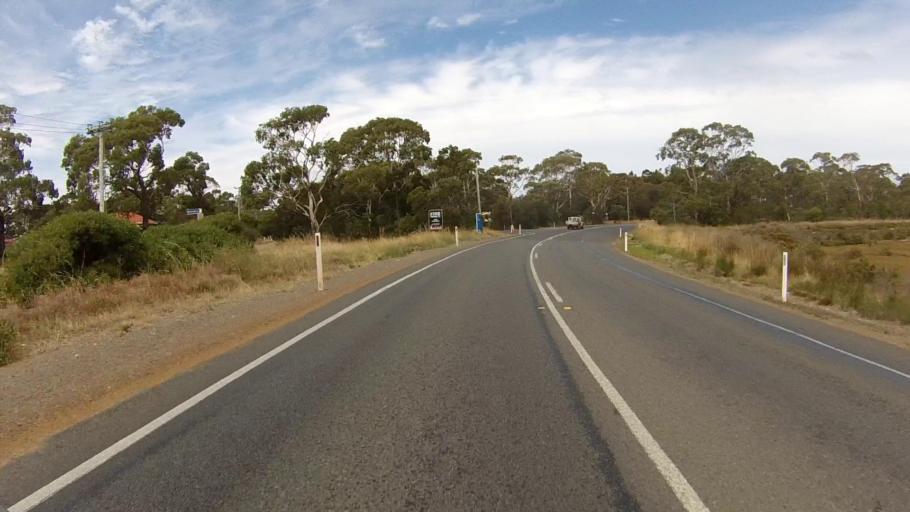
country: AU
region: Tasmania
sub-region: Clarence
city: Sandford
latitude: -42.9273
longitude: 147.4918
